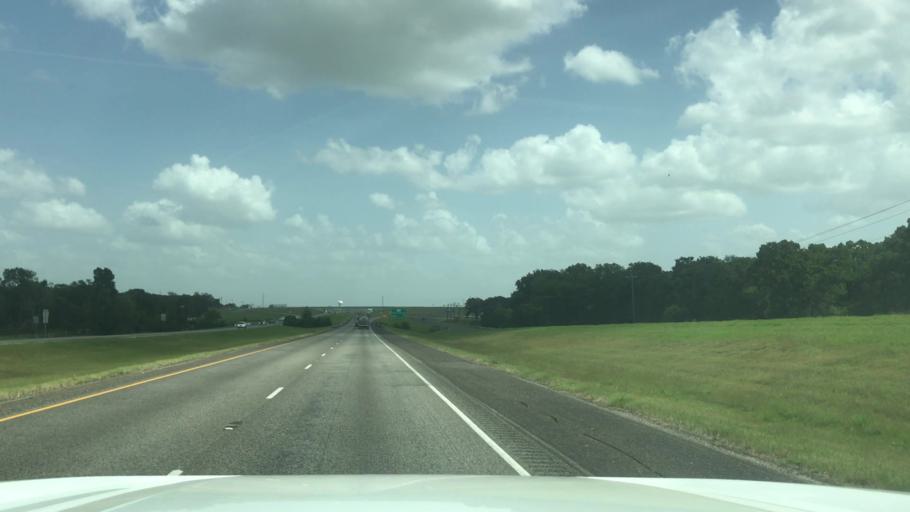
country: US
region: Texas
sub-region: Brazos County
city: Bryan
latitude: 30.7338
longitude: -96.4342
